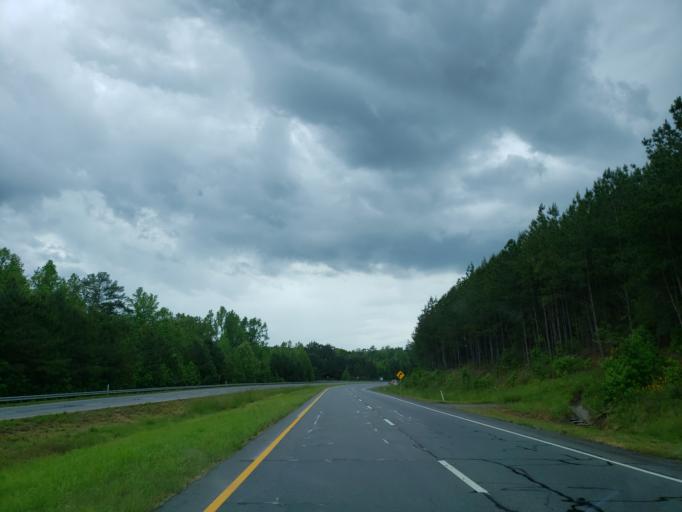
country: US
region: Georgia
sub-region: Haralson County
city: Buchanan
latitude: 33.8487
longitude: -85.2084
